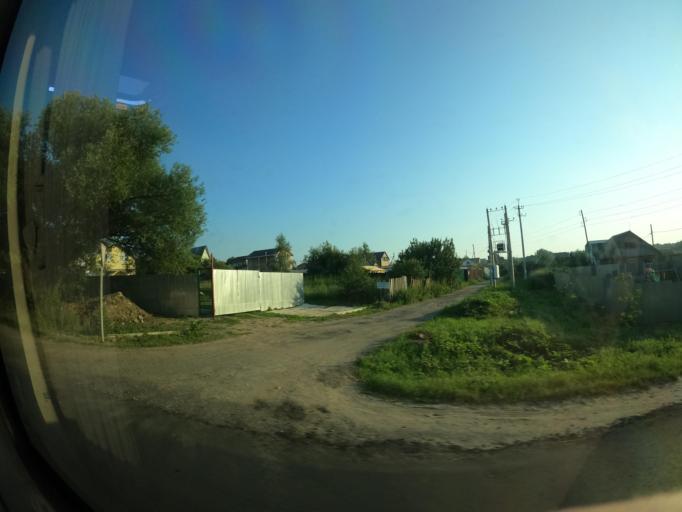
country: RU
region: Moskovskaya
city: Serpukhov
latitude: 54.9399
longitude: 37.3549
